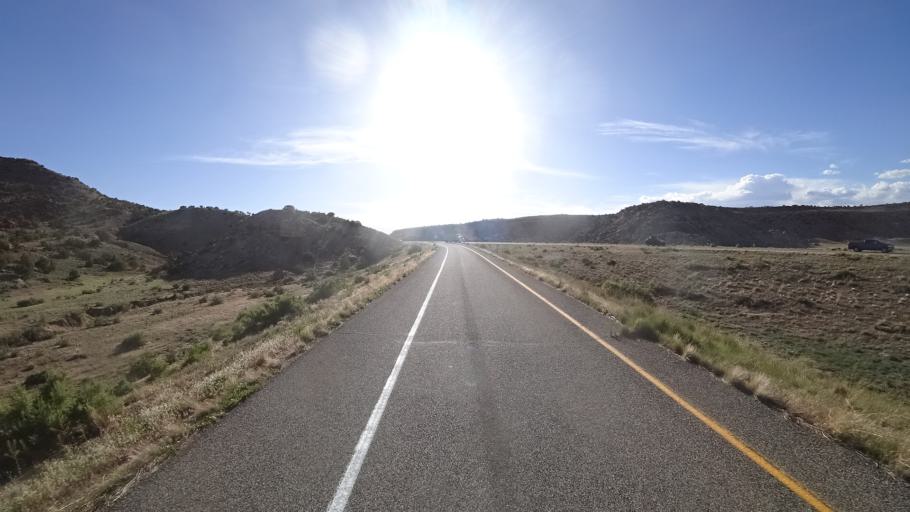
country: US
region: Colorado
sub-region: Mesa County
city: Loma
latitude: 39.1895
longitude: -109.0217
